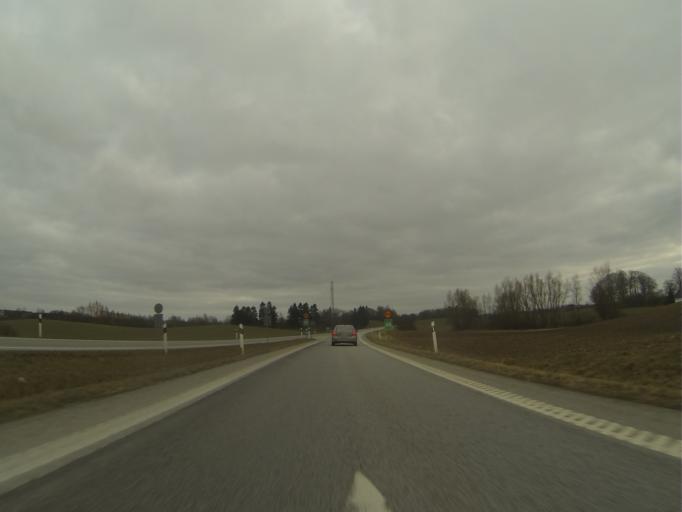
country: SE
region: Skane
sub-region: Svedala Kommun
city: Svedala
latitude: 55.5256
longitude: 13.2067
